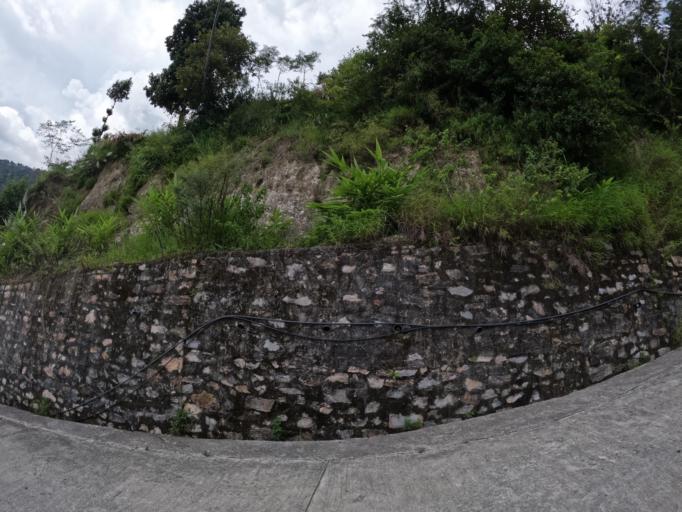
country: NP
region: Central Region
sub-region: Bagmati Zone
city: Kathmandu
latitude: 27.7763
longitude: 85.3406
